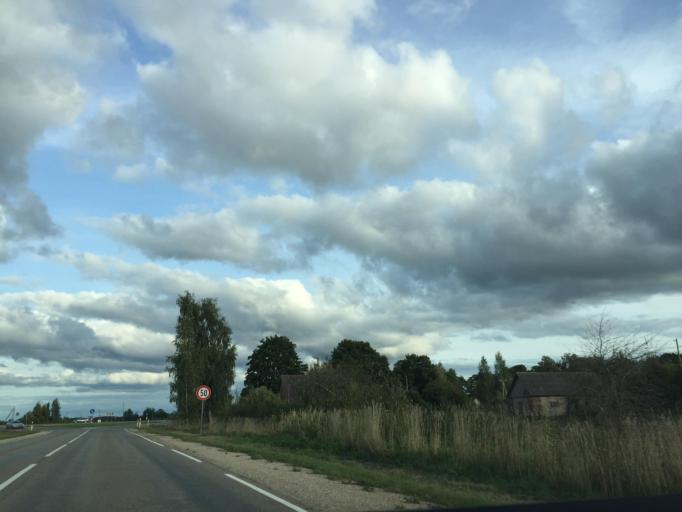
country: LV
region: Nereta
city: Nereta
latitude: 56.2532
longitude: 25.2141
